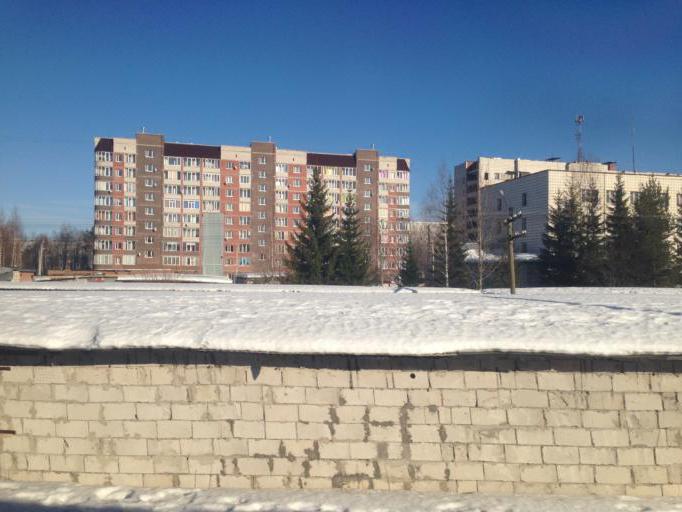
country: RU
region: Komi Republic
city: Ezhva
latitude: 61.7880
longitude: 50.7390
